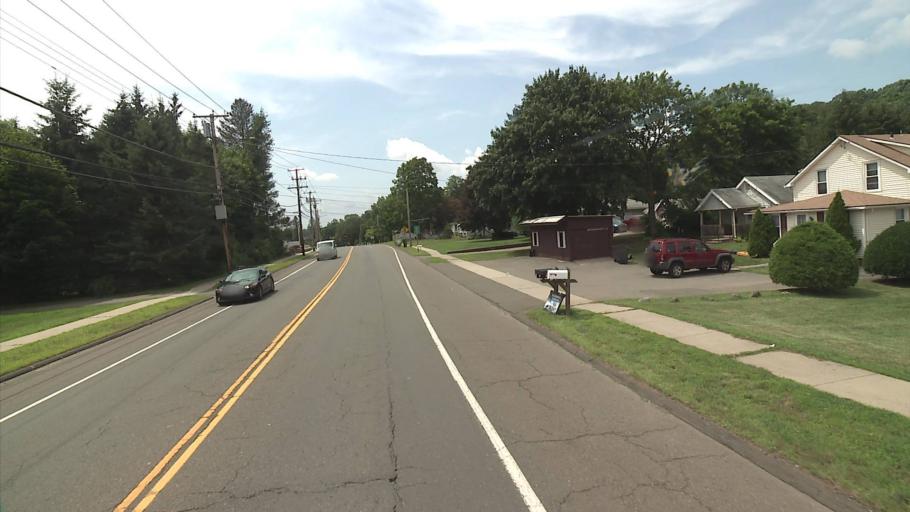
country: US
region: Connecticut
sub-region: New Haven County
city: Branford
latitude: 41.3249
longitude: -72.8304
